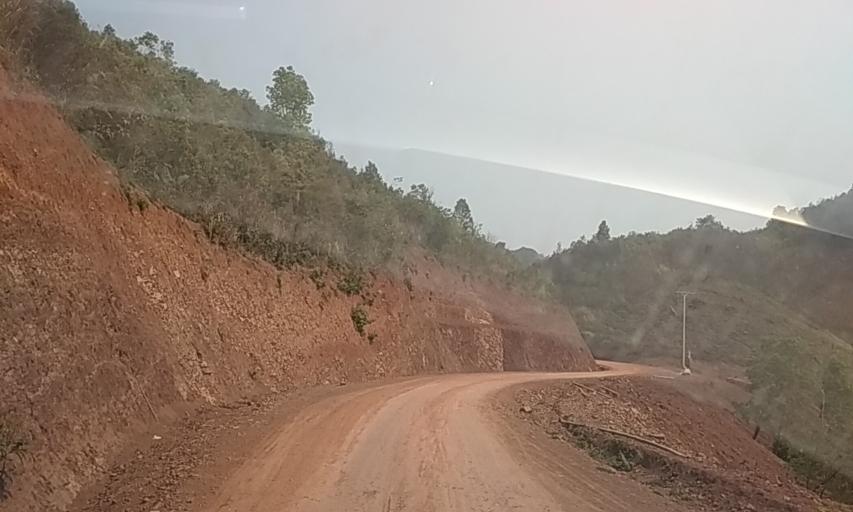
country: VN
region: Huyen Dien Bien
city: Dien Bien Phu
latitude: 21.4762
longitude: 102.7765
